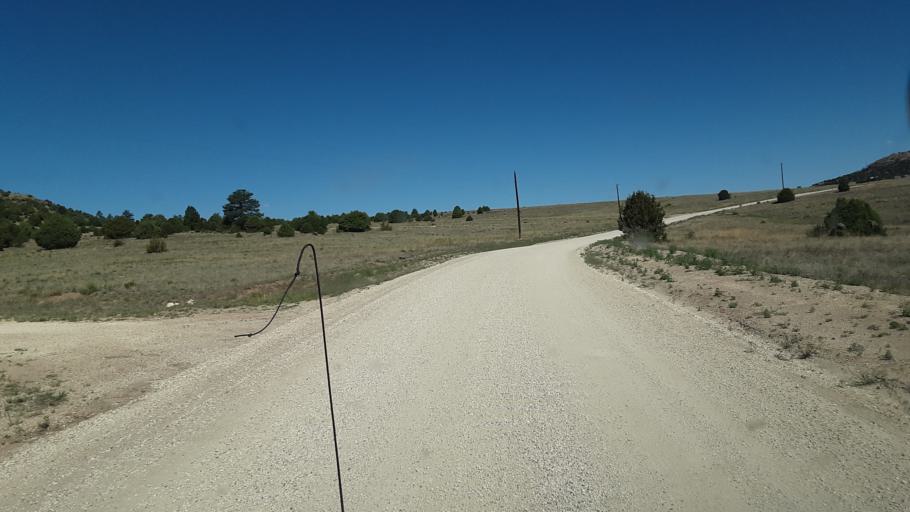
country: US
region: Colorado
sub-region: Custer County
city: Westcliffe
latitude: 38.2207
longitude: -105.4568
